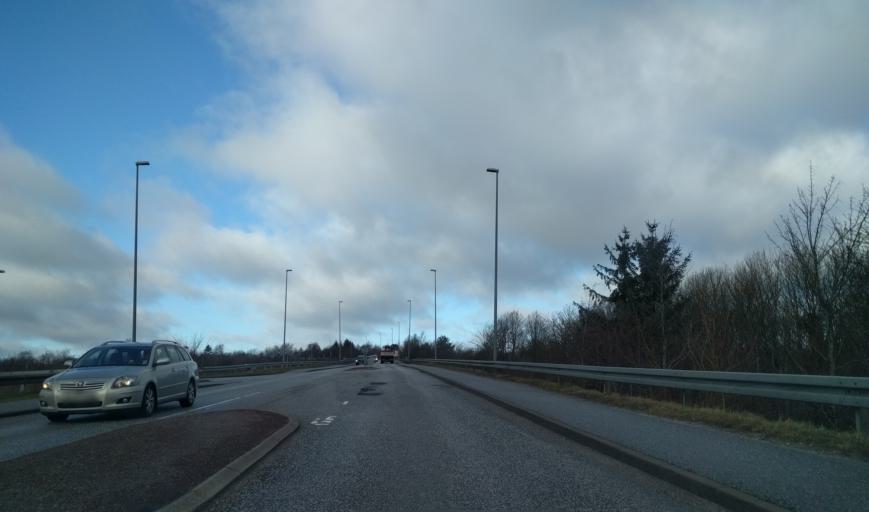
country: DK
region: North Denmark
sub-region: Alborg Kommune
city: Aalborg
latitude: 57.0115
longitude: 9.9074
